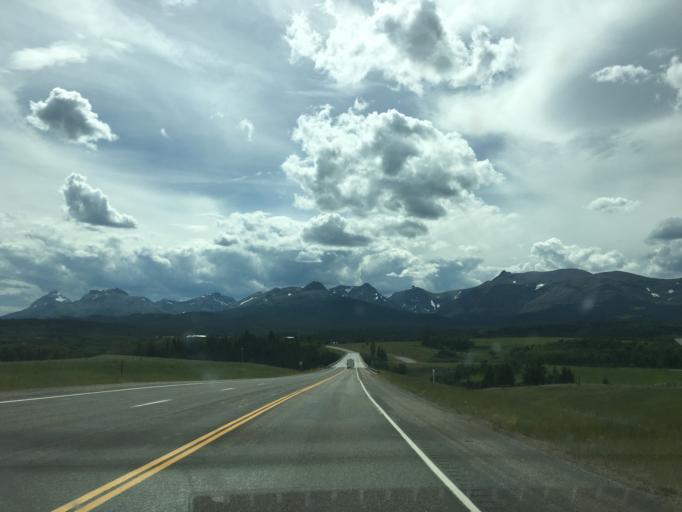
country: US
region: Montana
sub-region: Glacier County
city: South Browning
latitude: 48.4511
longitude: -113.1990
